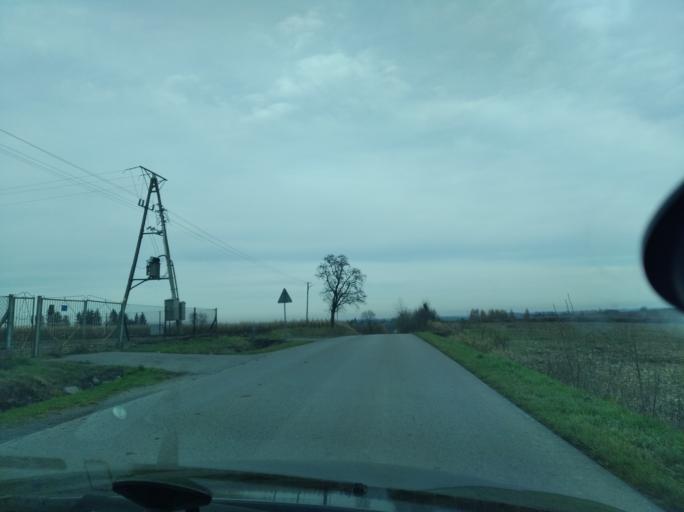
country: PL
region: Subcarpathian Voivodeship
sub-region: Powiat przeworski
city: Debow
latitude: 50.0394
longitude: 22.4274
